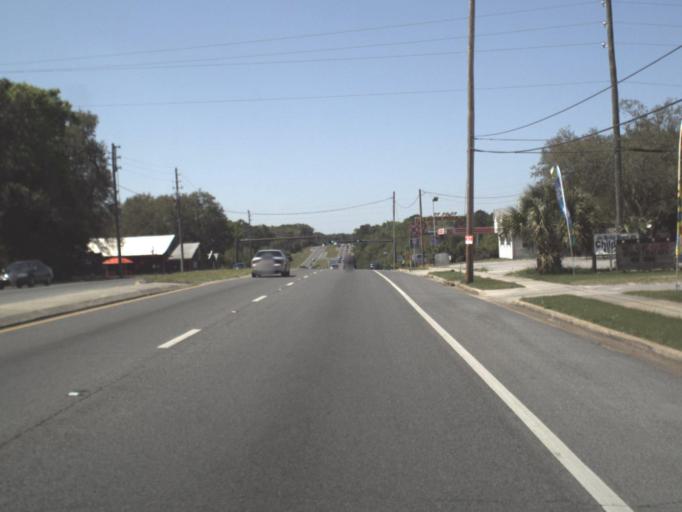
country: US
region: Florida
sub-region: Escambia County
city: West Pensacola
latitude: 30.4452
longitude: -87.2871
